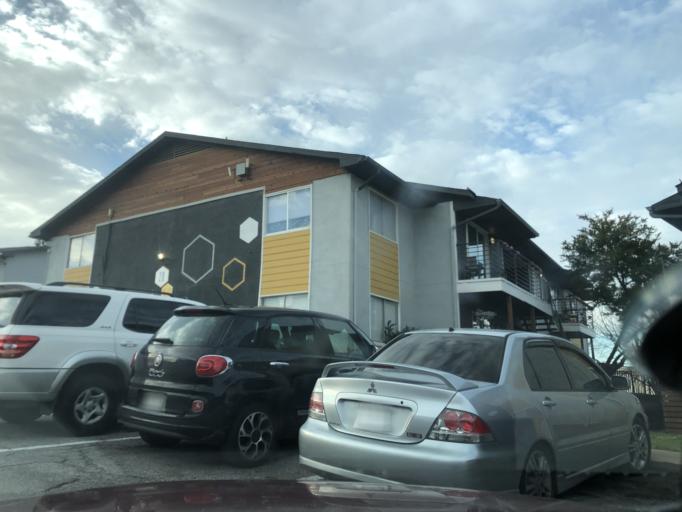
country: US
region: Texas
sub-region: Dallas County
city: Highland Park
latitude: 32.8600
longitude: -96.7492
